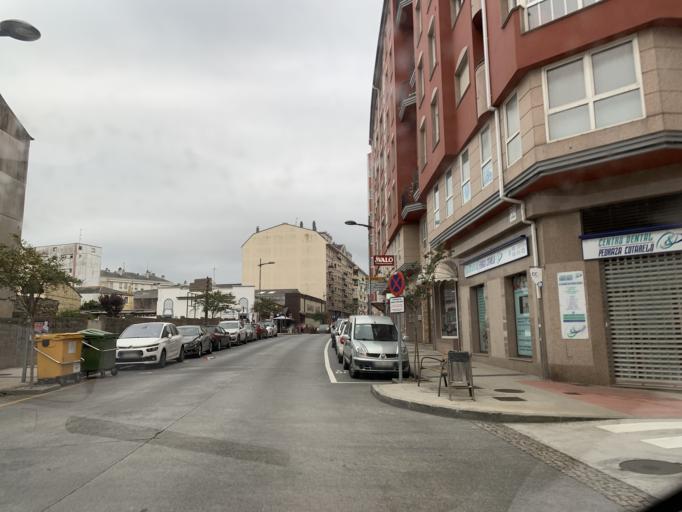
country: ES
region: Galicia
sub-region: Provincia de Lugo
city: Ribadeo
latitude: 43.5356
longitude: -7.0429
